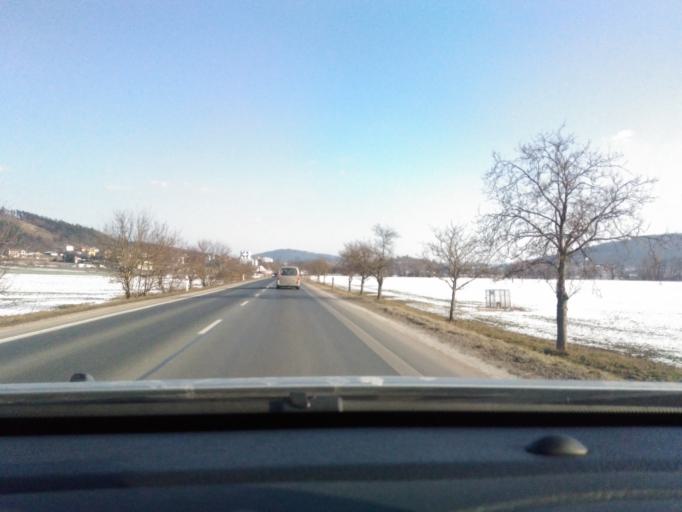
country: CZ
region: South Moravian
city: Tisnov
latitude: 49.3391
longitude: 16.4251
